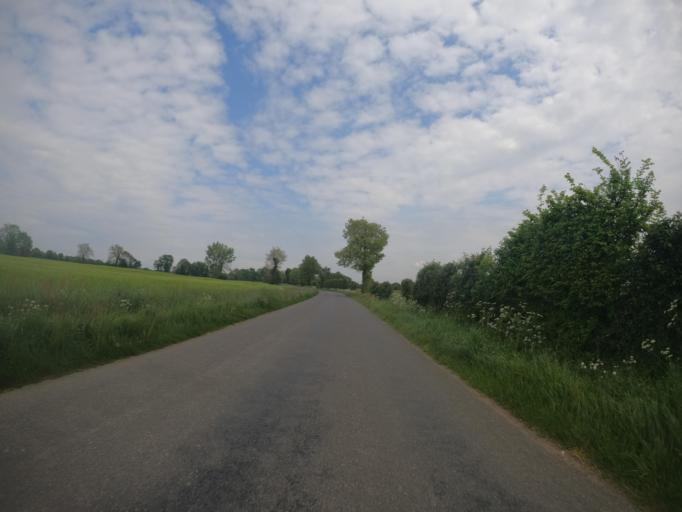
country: FR
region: Poitou-Charentes
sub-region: Departement des Deux-Sevres
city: Saint-Varent
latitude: 46.8782
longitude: -0.2711
